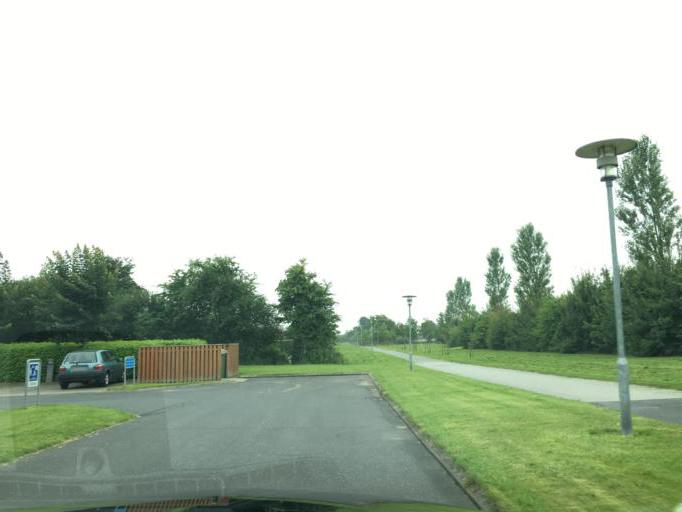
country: DK
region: South Denmark
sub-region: Kolding Kommune
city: Kolding
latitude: 55.5614
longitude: 9.4848
